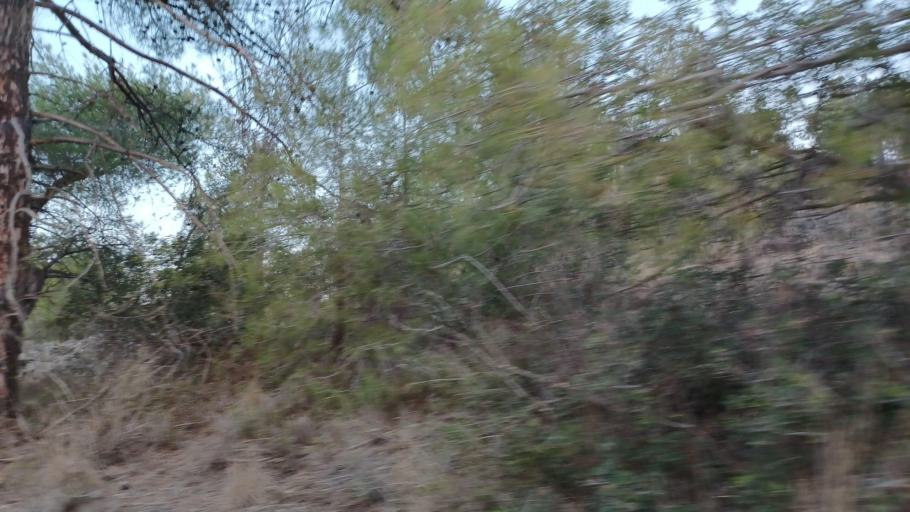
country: CY
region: Larnaka
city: Kornos
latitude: 34.9100
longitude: 33.3543
